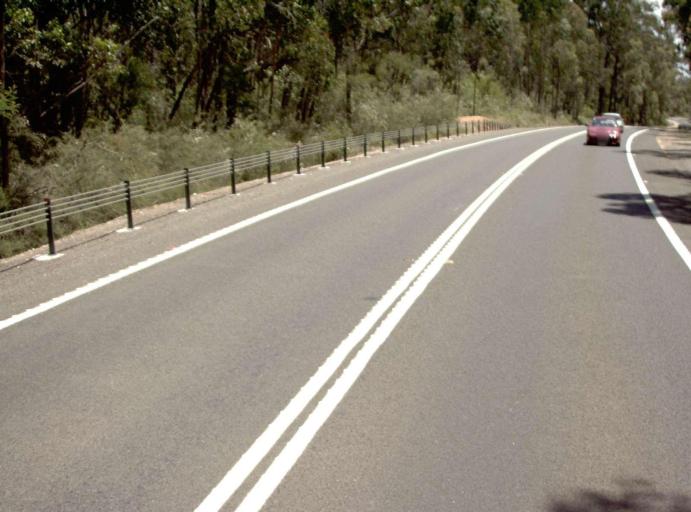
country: AU
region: Victoria
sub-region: East Gippsland
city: Lakes Entrance
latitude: -37.7023
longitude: 148.5829
